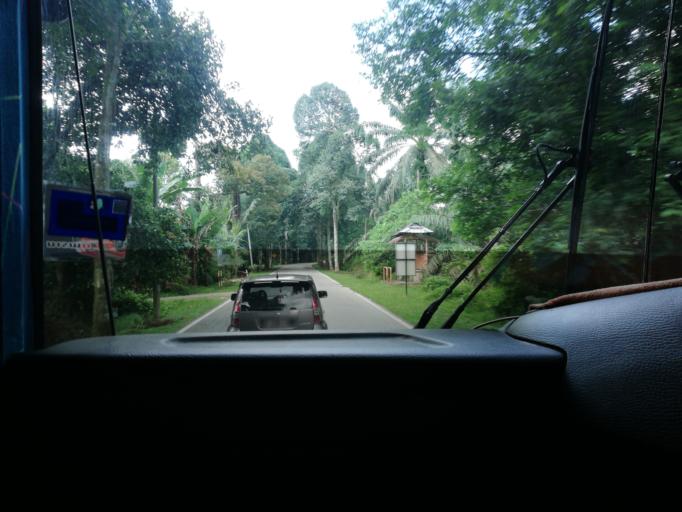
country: MY
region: Kedah
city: Kulim
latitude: 5.2468
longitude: 100.6025
